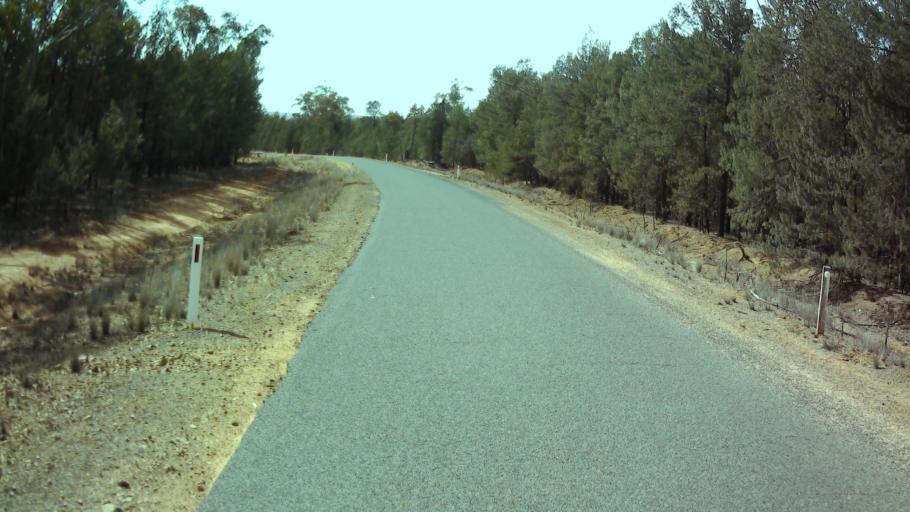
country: AU
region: New South Wales
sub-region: Weddin
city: Grenfell
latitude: -33.7482
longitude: 148.0570
